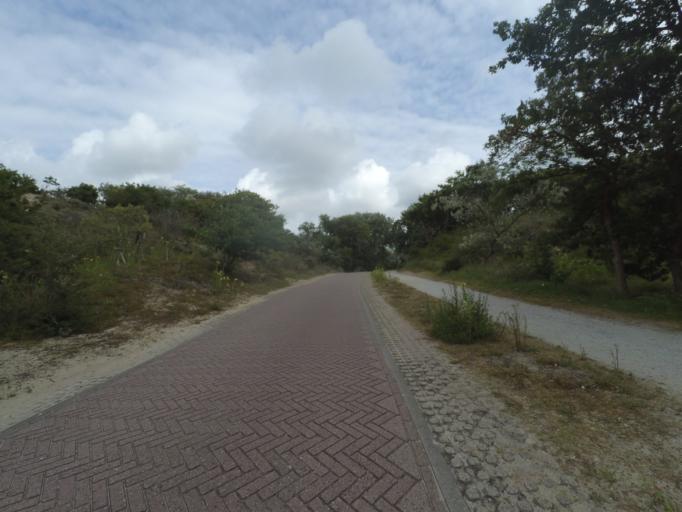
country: NL
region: South Holland
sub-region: Gemeente Den Haag
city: Scheveningen
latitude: 52.1304
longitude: 4.3306
